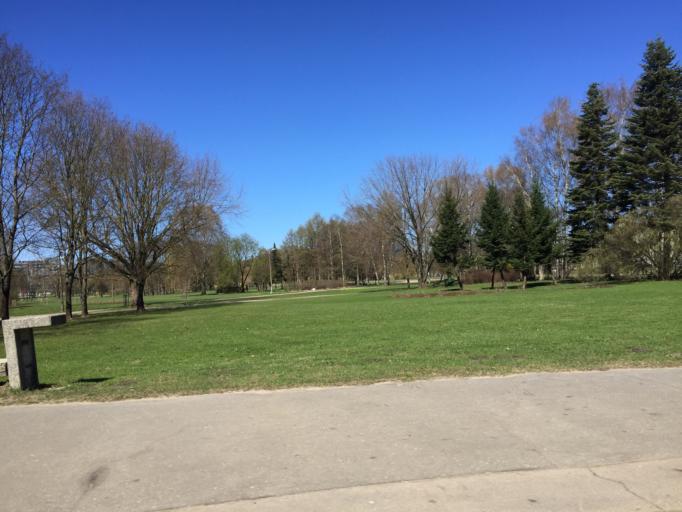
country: LV
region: Riga
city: Riga
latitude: 56.9392
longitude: 24.0900
